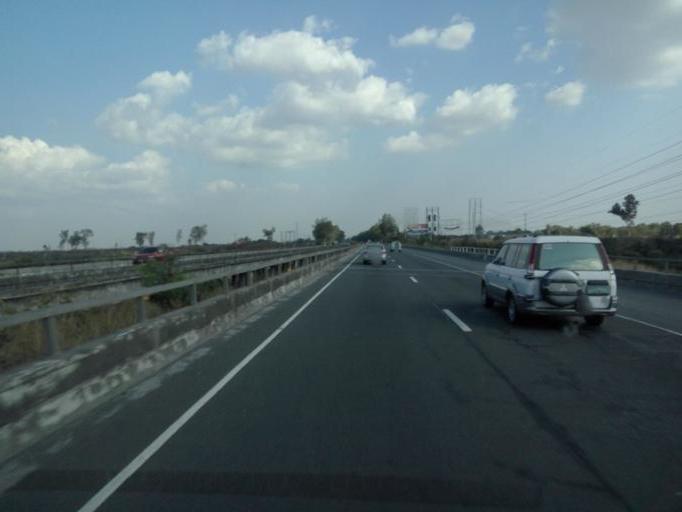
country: PH
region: Central Luzon
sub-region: Province of Pampanga
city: Balibago
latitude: 15.1506
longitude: 120.6228
